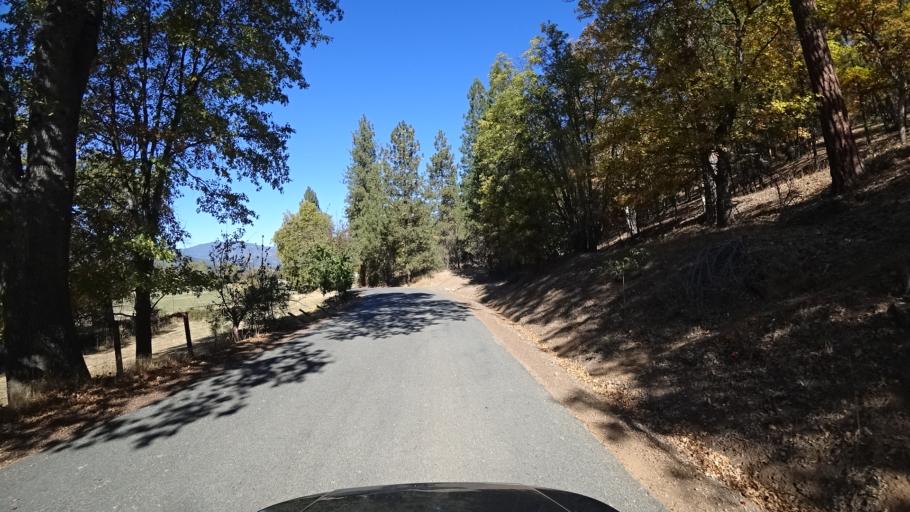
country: US
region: California
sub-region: Siskiyou County
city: Yreka
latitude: 41.5794
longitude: -122.9575
